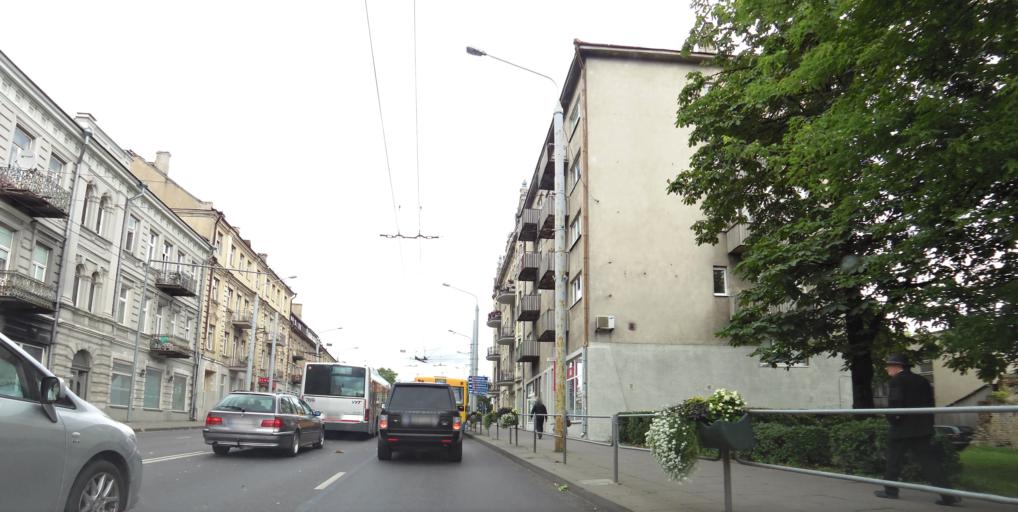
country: LT
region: Vilnius County
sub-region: Vilnius
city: Vilnius
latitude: 54.6935
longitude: 25.2812
